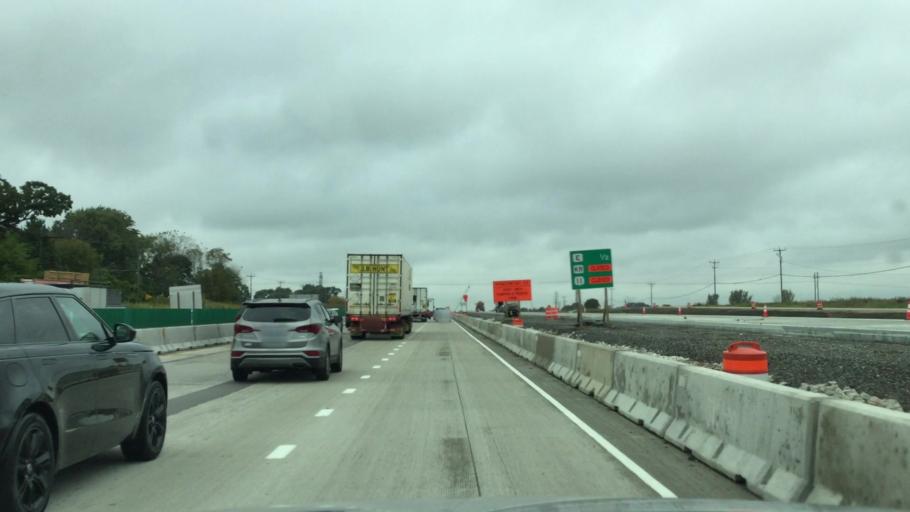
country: US
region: Wisconsin
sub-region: Kenosha County
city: Somers
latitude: 42.6285
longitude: -87.9525
